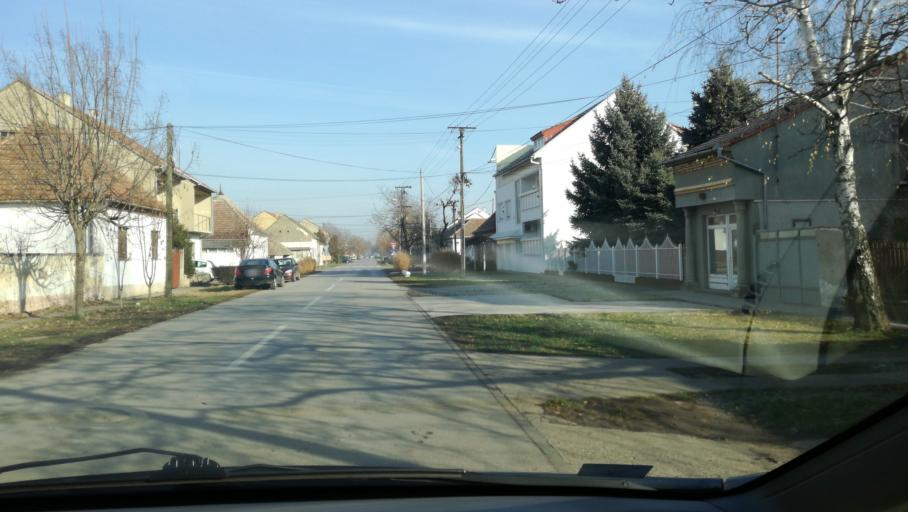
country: RS
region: Autonomna Pokrajina Vojvodina
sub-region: Severnobanatski Okrug
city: Kikinda
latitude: 45.8234
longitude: 20.4524
